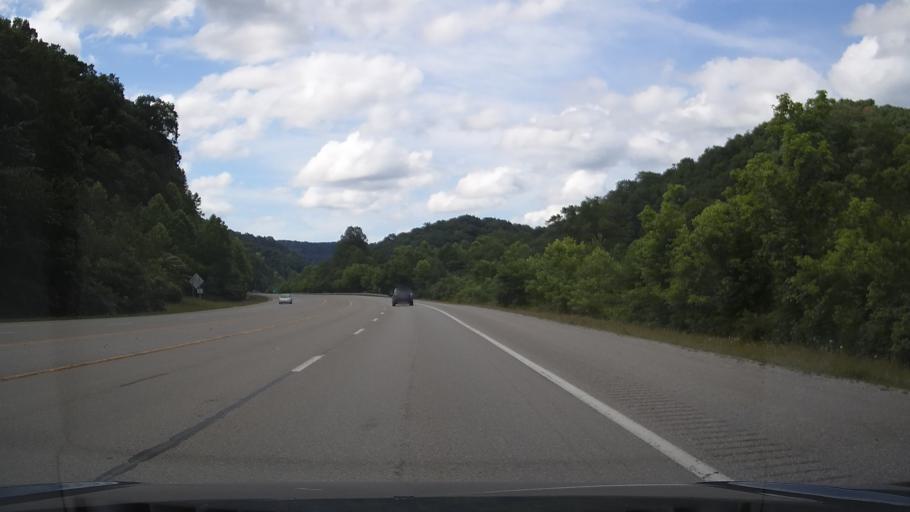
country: US
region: Kentucky
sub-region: Johnson County
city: Van Lear
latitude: 37.7286
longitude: -82.7870
